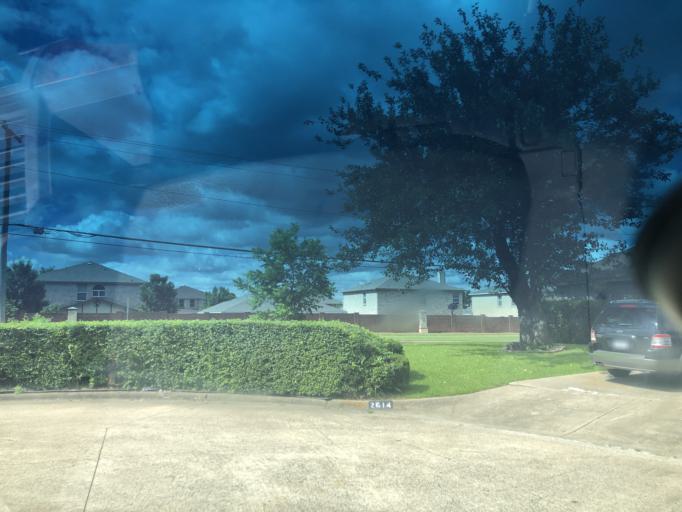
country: US
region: Texas
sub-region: Dallas County
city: Grand Prairie
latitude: 32.7065
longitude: -97.0399
